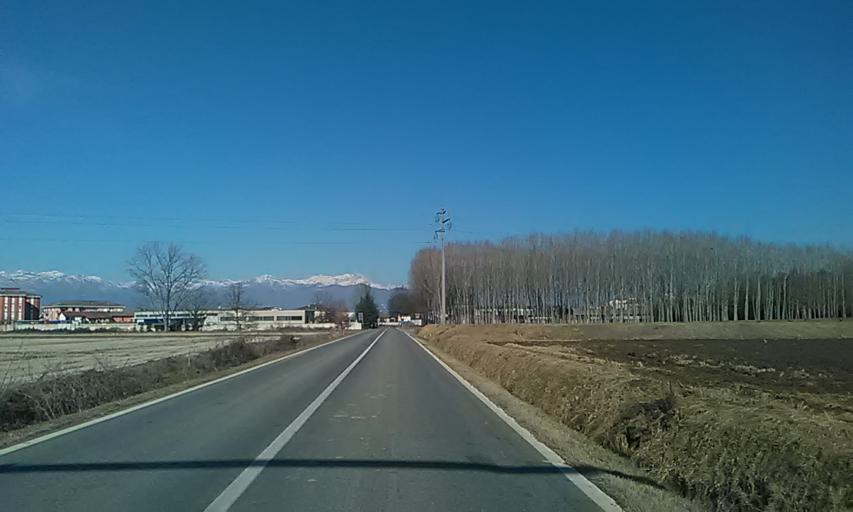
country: IT
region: Piedmont
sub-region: Provincia di Vercelli
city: Buronzo
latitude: 45.4742
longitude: 8.2676
